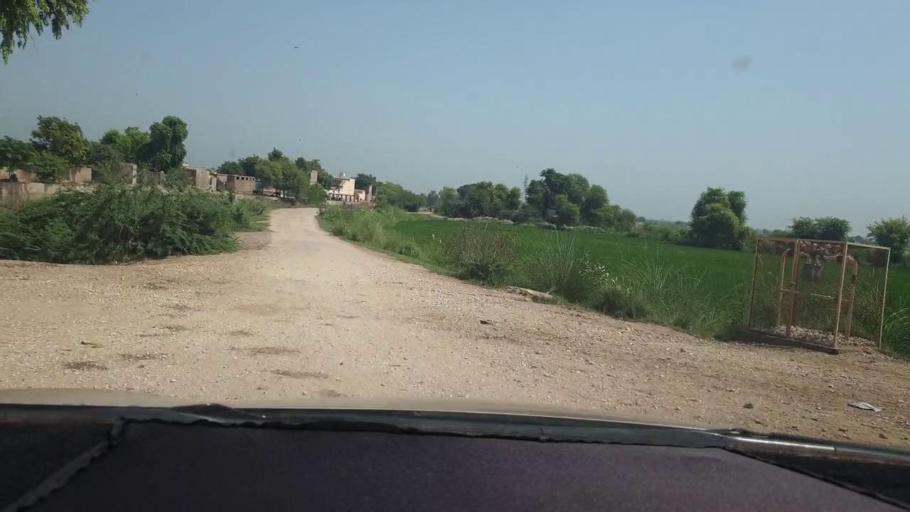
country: PK
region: Sindh
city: Kambar
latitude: 27.5859
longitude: 68.0595
